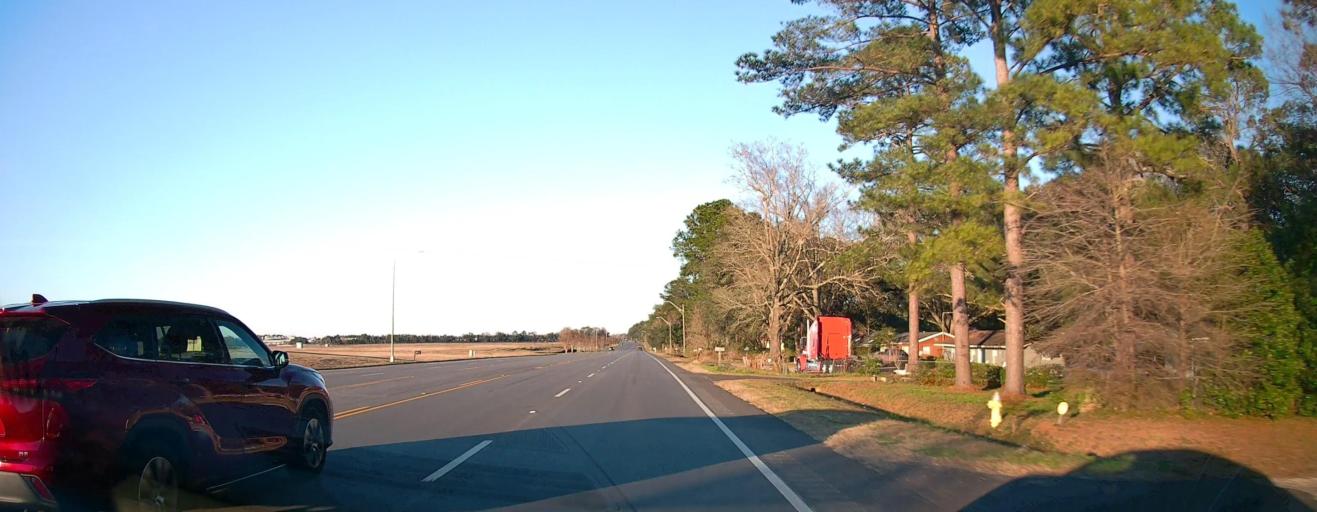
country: US
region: Georgia
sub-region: Dougherty County
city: Albany
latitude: 31.5357
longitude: -84.1844
